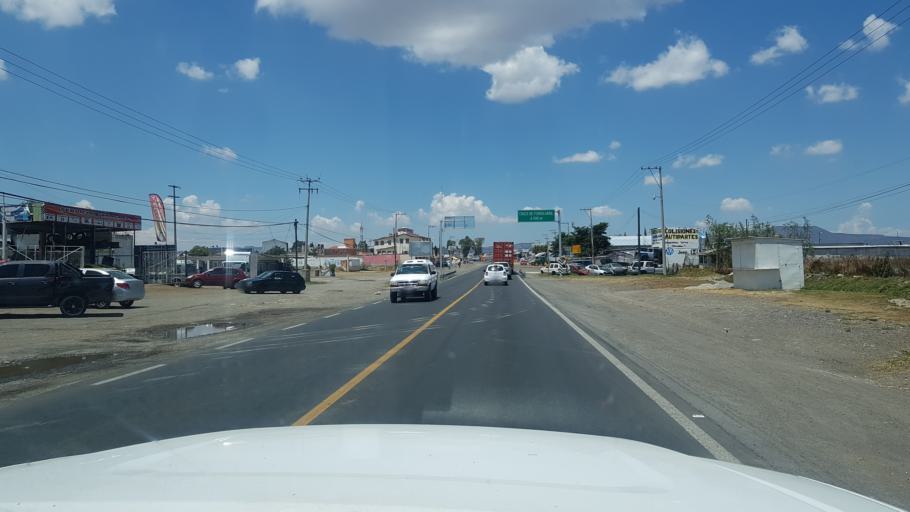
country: MX
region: Hidalgo
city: Calpulalpan
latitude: 19.5903
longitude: -98.5565
